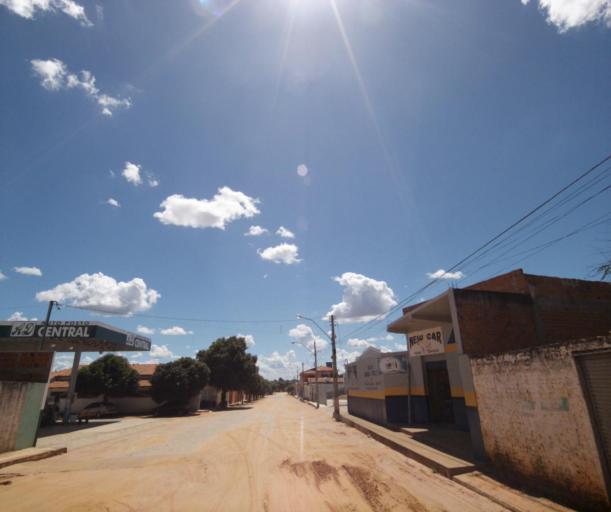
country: BR
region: Bahia
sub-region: Carinhanha
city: Carinhanha
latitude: -14.2118
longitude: -44.2798
